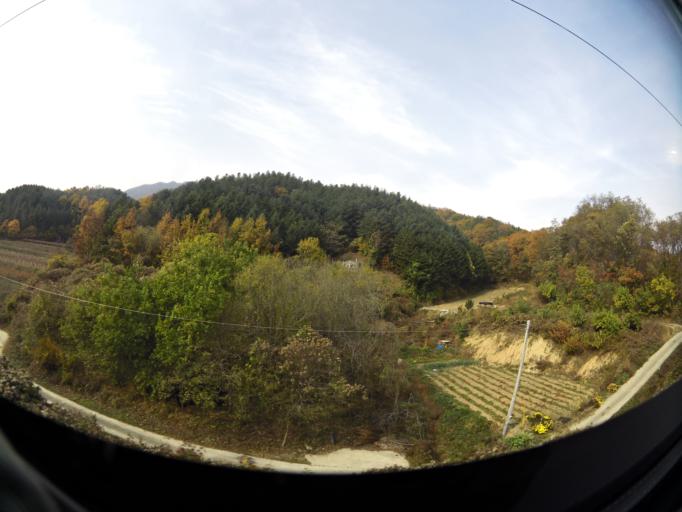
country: KR
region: Gyeongsangbuk-do
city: Gimcheon
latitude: 36.1787
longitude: 128.0073
